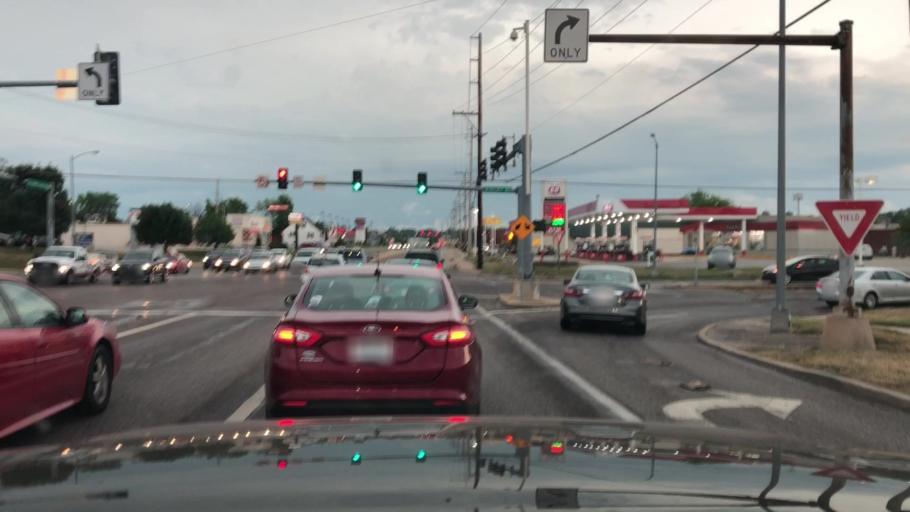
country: US
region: Missouri
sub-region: Saint Louis County
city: Bridgeton
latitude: 38.7514
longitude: -90.4267
